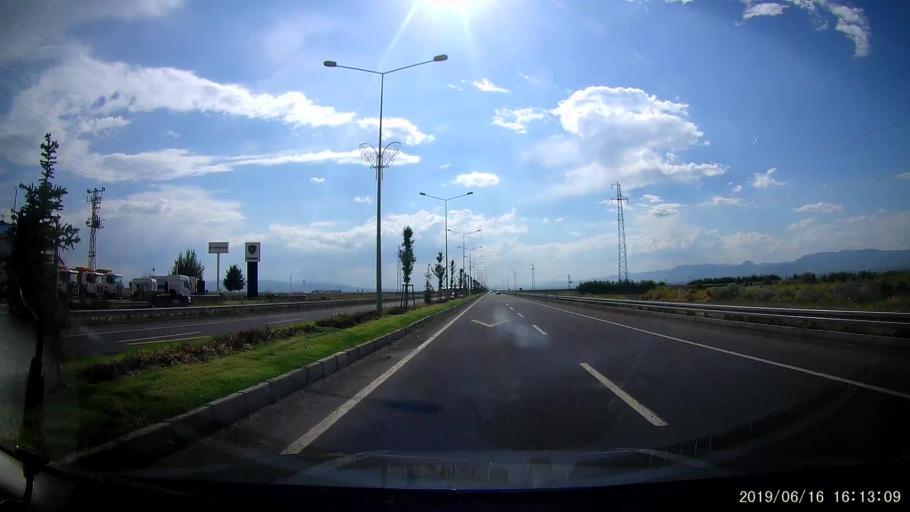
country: TR
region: Erzurum
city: Erzurum
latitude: 39.9593
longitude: 41.2774
